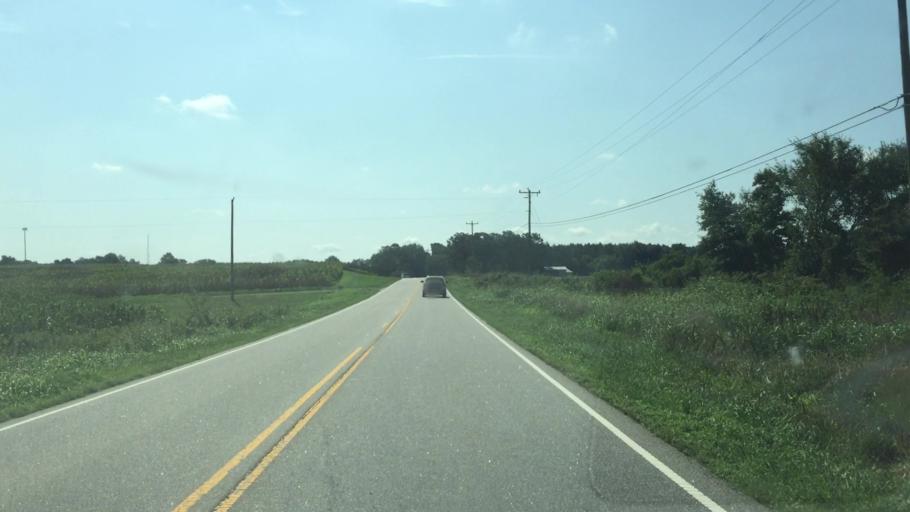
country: US
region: North Carolina
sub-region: Stanly County
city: Oakboro
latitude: 35.1260
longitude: -80.3590
